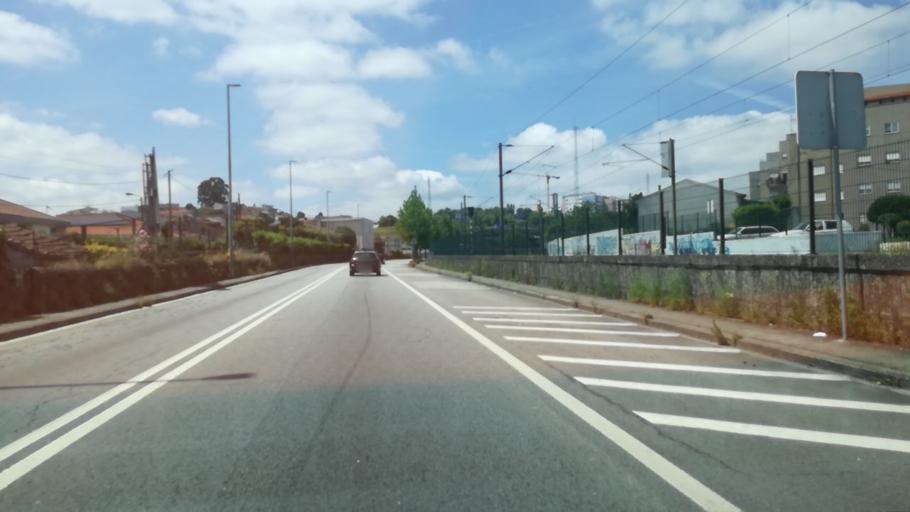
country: PT
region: Braga
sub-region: Braga
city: Braga
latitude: 41.5322
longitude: -8.4396
